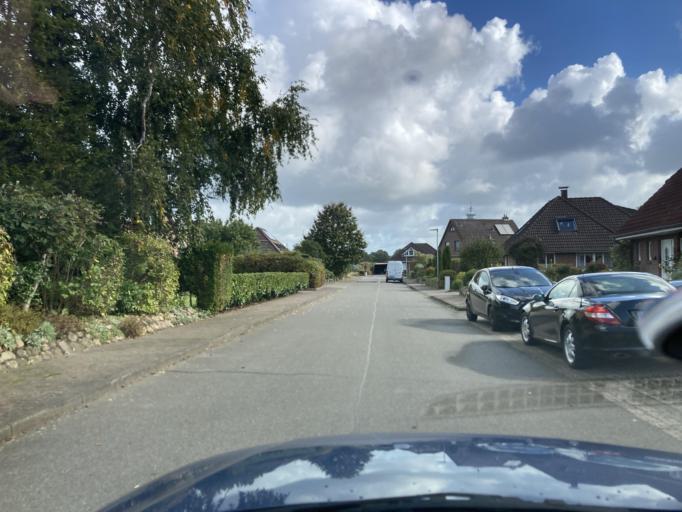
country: DE
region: Schleswig-Holstein
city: Wesseln
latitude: 54.2072
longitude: 9.0791
